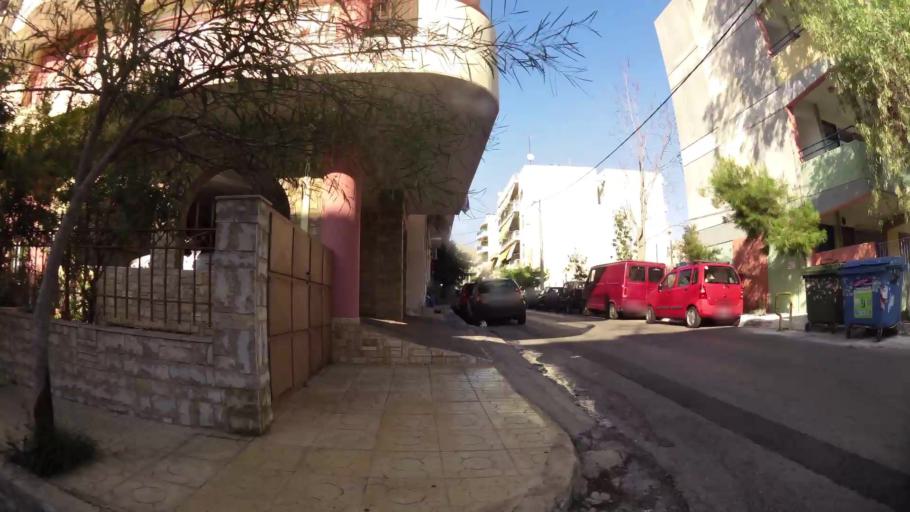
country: GR
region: Attica
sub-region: Nomos Piraios
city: Keratsini
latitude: 37.9737
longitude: 23.6261
